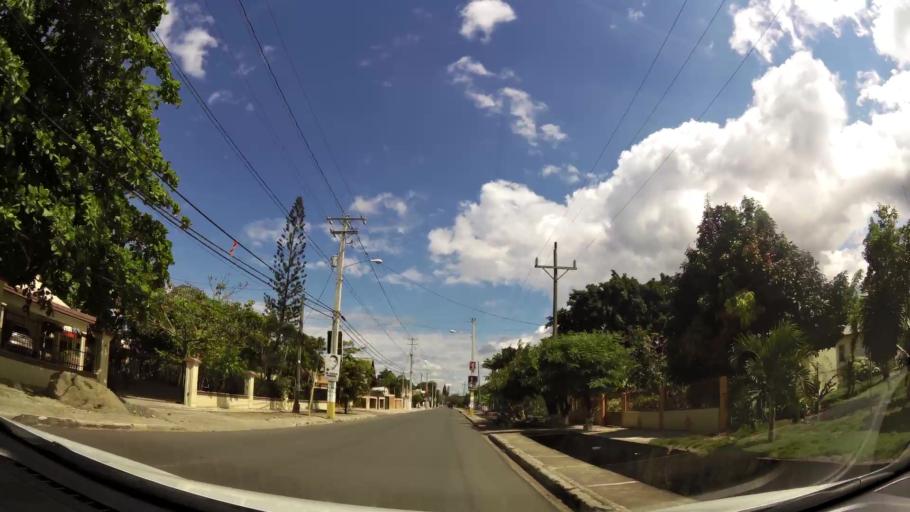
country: DO
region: Santiago
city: Licey al Medio
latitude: 19.3843
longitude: -70.6248
